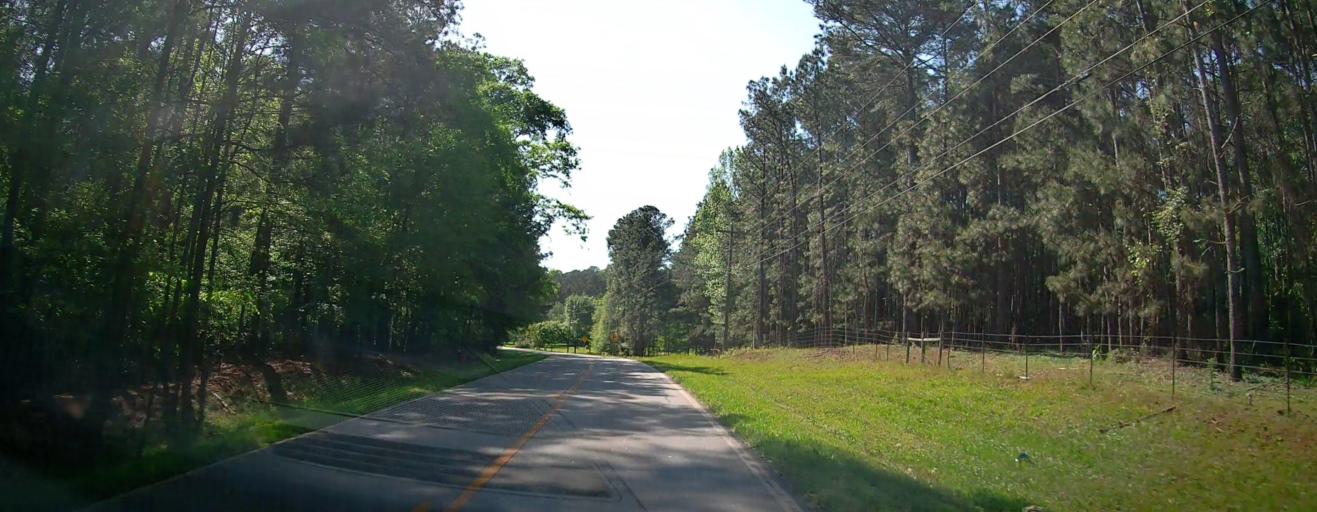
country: US
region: Georgia
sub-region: Morgan County
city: Madison
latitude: 33.6555
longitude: -83.4531
